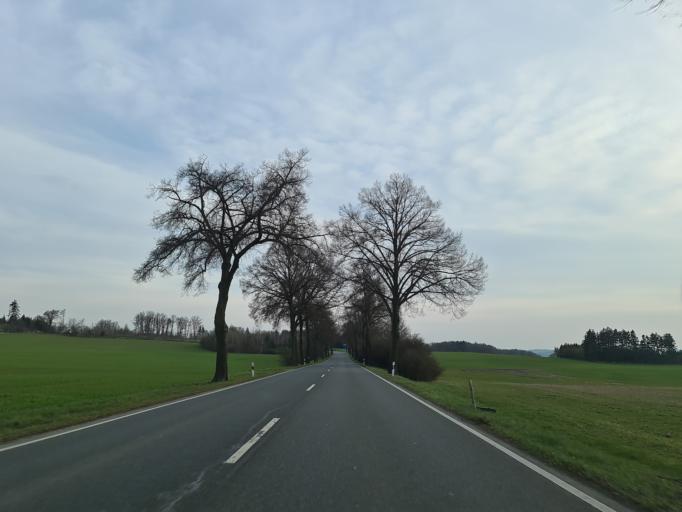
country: DE
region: Saxony
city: Oelsnitz
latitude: 50.4488
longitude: 12.1610
